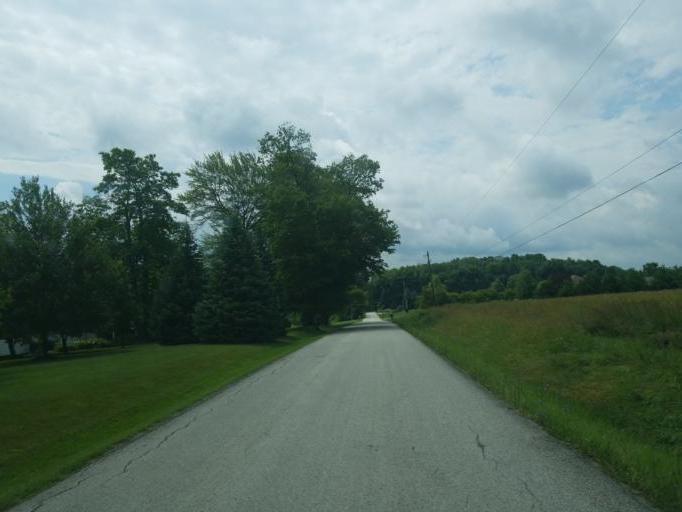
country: US
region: Ohio
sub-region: Richland County
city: Ontario
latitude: 40.7221
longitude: -82.6263
